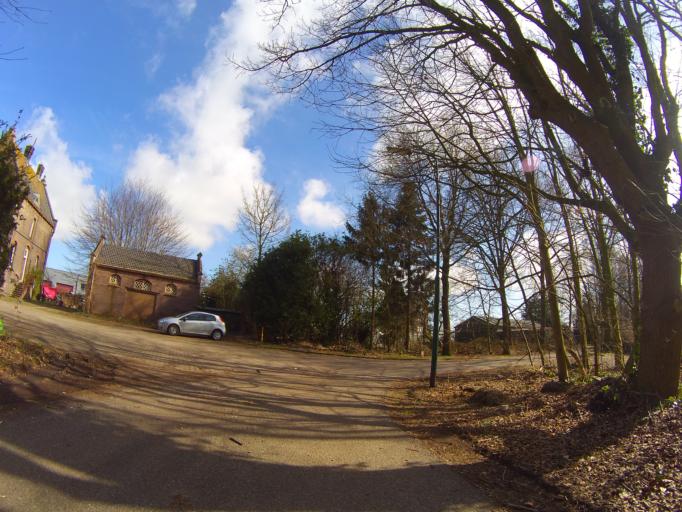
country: NL
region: Utrecht
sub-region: Gemeente Woudenberg
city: Woudenberg
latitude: 52.0815
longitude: 5.4485
